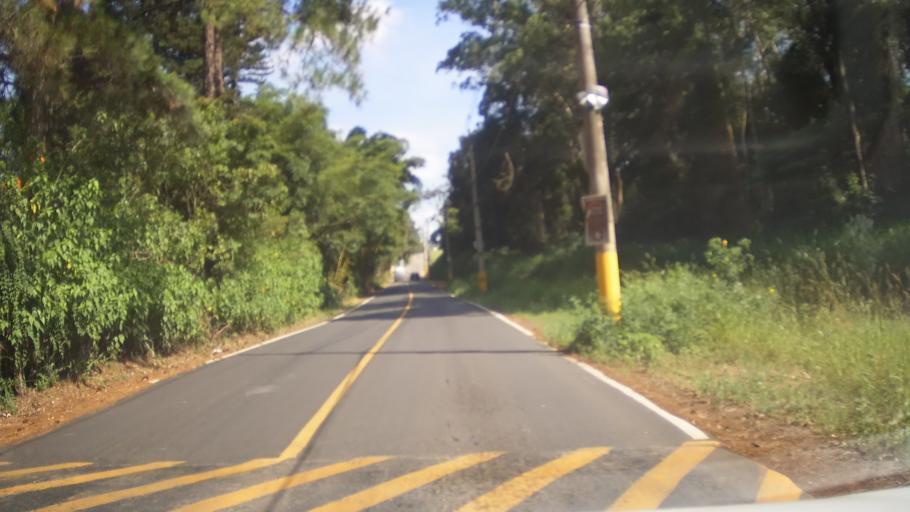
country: BR
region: Sao Paulo
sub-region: Itupeva
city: Itupeva
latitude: -23.2001
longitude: -47.0685
